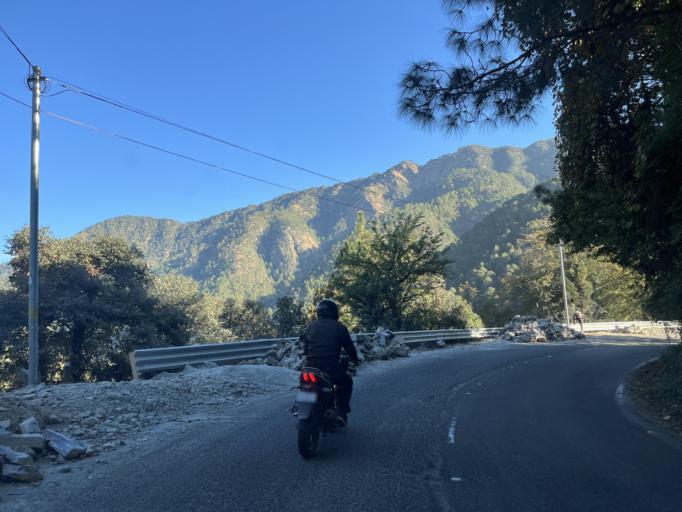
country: IN
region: Uttarakhand
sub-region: Naini Tal
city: Bhowali
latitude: 29.4077
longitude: 79.5142
